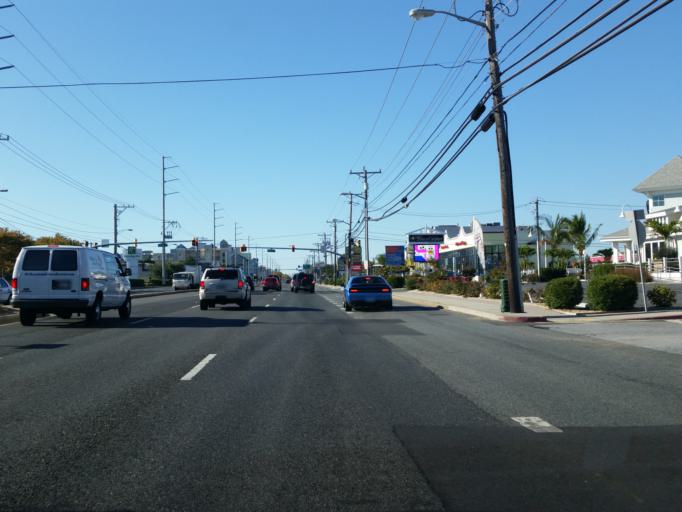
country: US
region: Maryland
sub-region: Worcester County
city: Ocean City
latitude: 38.3900
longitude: -75.0649
